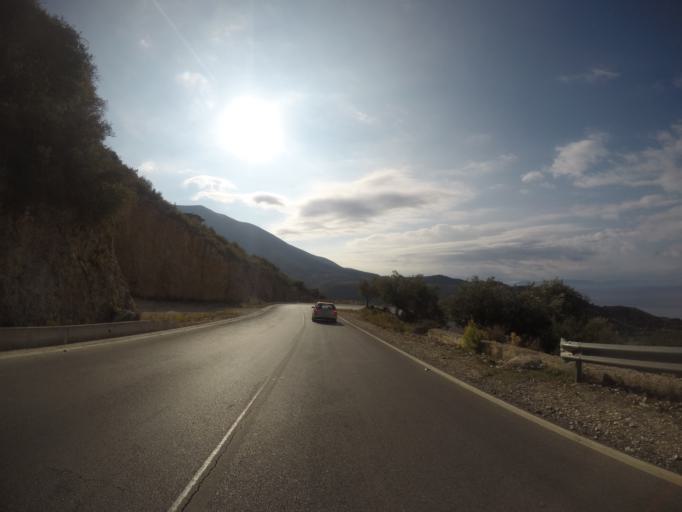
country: AL
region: Vlore
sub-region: Rrethi i Sarandes
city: Lukove
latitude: 40.0134
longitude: 19.8988
